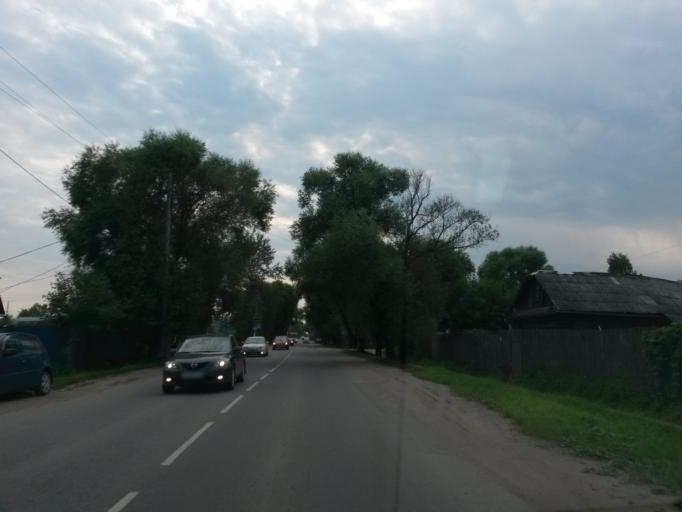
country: RU
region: Jaroslavl
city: Yaroslavl
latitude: 57.6063
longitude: 39.8077
